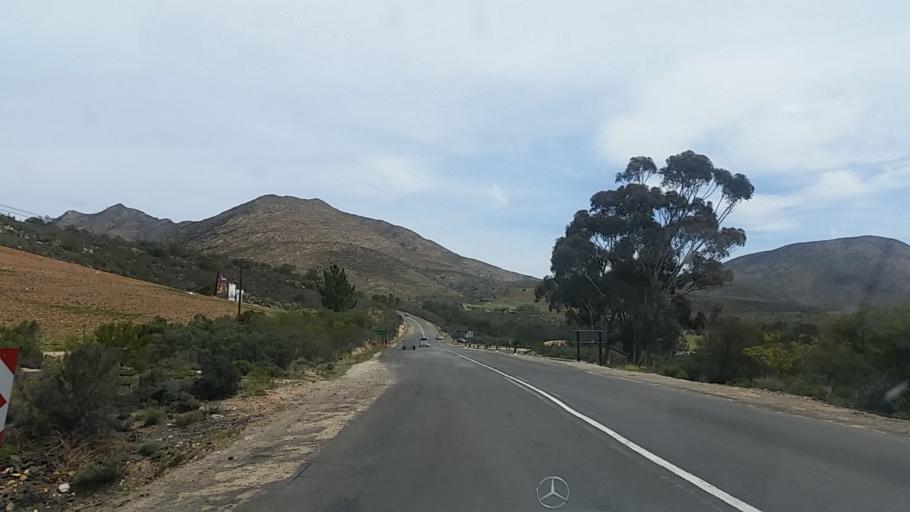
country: ZA
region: Western Cape
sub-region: Eden District Municipality
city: George
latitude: -33.8191
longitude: 22.3565
